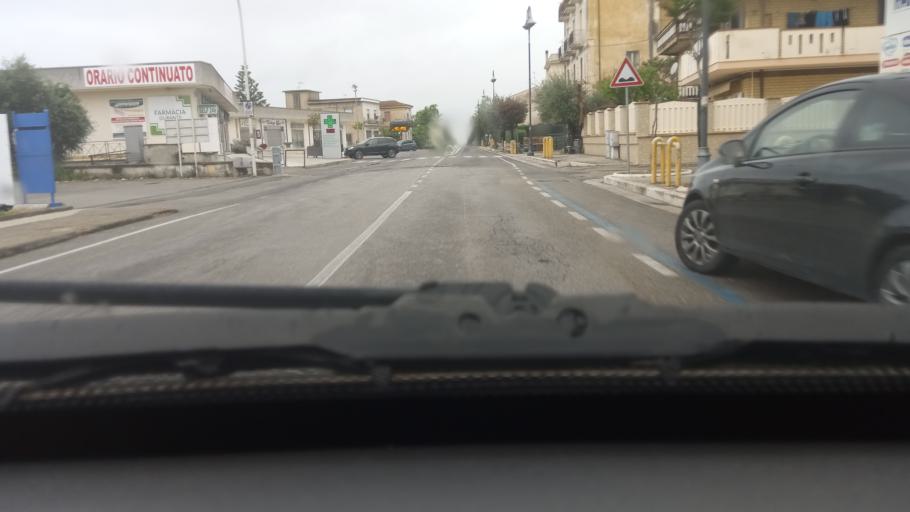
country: IT
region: Latium
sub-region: Provincia di Latina
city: Minturno
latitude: 41.2494
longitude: 13.7388
